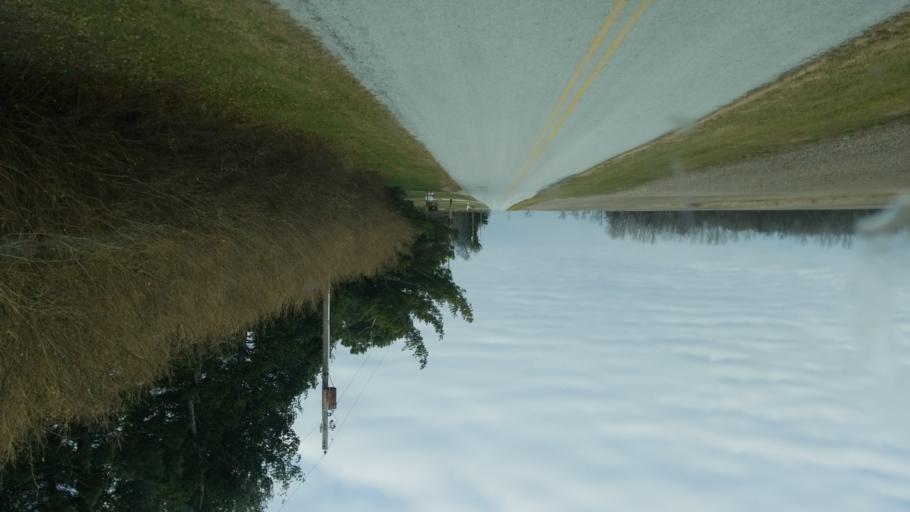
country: US
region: Ohio
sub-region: Hardin County
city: Kenton
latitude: 40.6136
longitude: -83.4202
